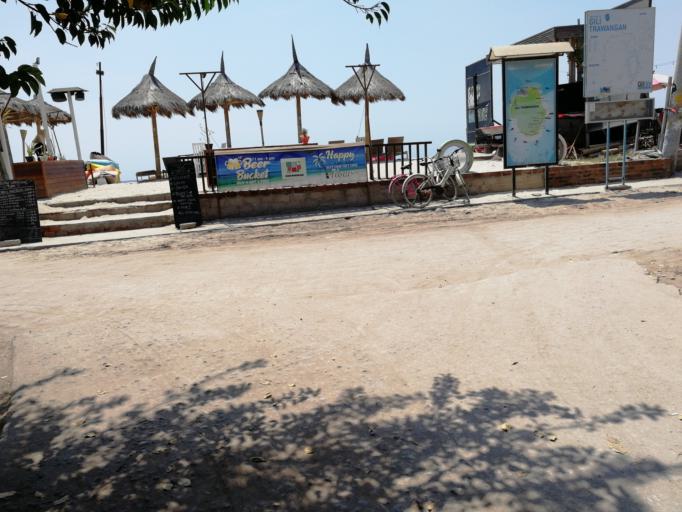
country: ID
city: Gili Trawangan
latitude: -8.3448
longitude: 116.0289
